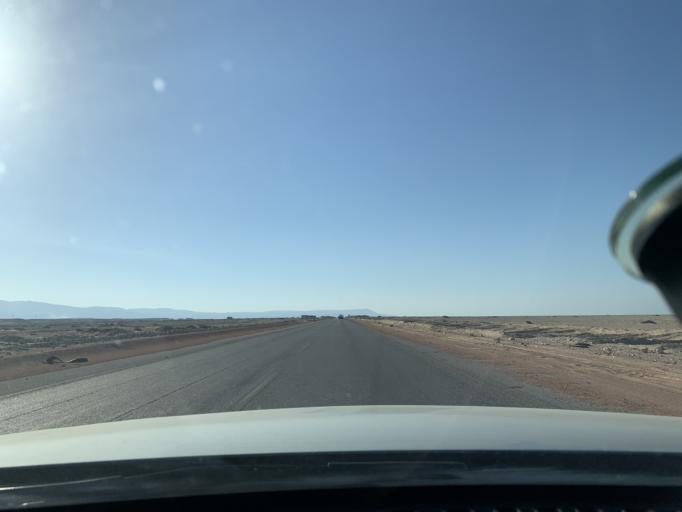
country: EG
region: As Suways
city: Ain Sukhna
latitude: 28.8221
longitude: 32.7236
